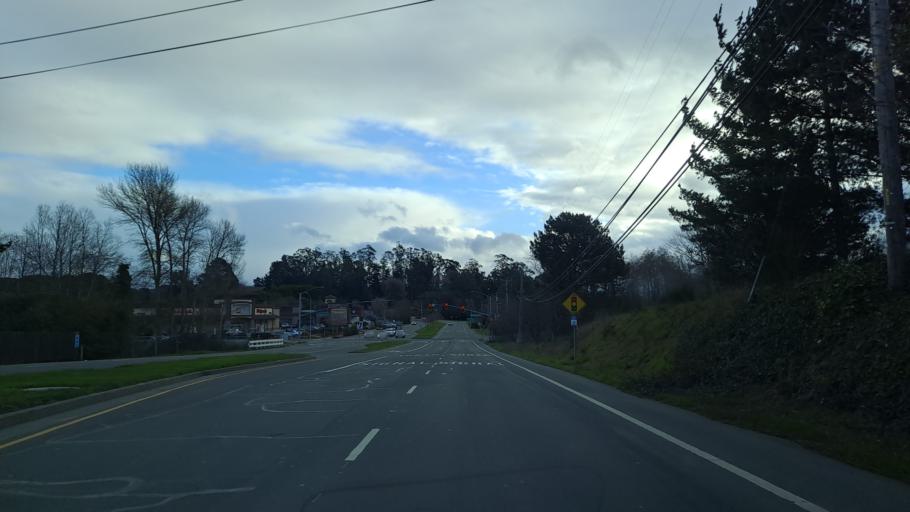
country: US
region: California
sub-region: Humboldt County
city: Fortuna
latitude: 40.5811
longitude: -124.1469
